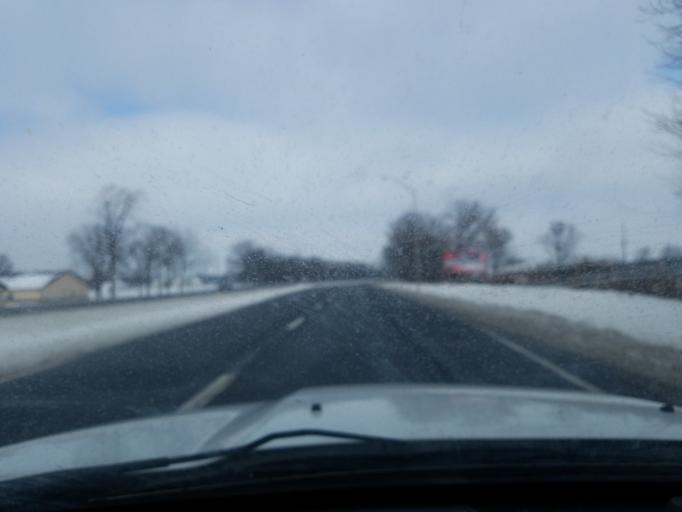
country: US
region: Indiana
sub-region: Marshall County
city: Plymouth
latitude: 41.3416
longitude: -86.2761
